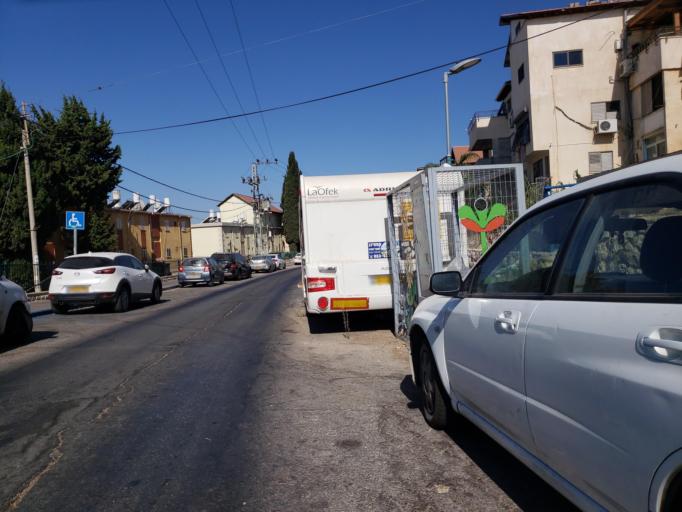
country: IL
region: Northern District
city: Safed
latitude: 32.9561
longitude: 35.4972
